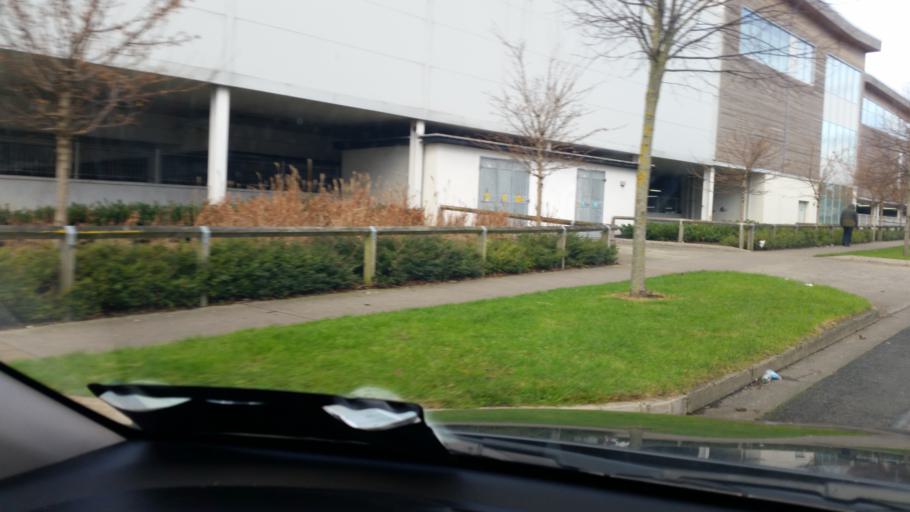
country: IE
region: Leinster
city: Cabra
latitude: 53.3597
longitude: -6.2994
